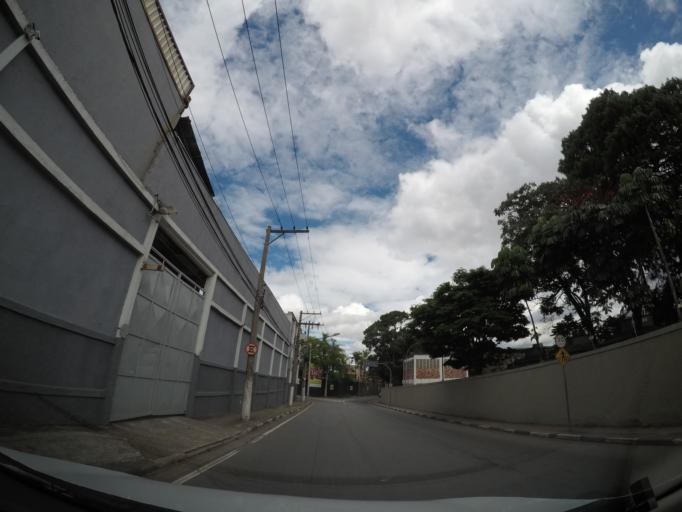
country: BR
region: Sao Paulo
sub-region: Guarulhos
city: Guarulhos
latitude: -23.4922
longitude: -46.5540
